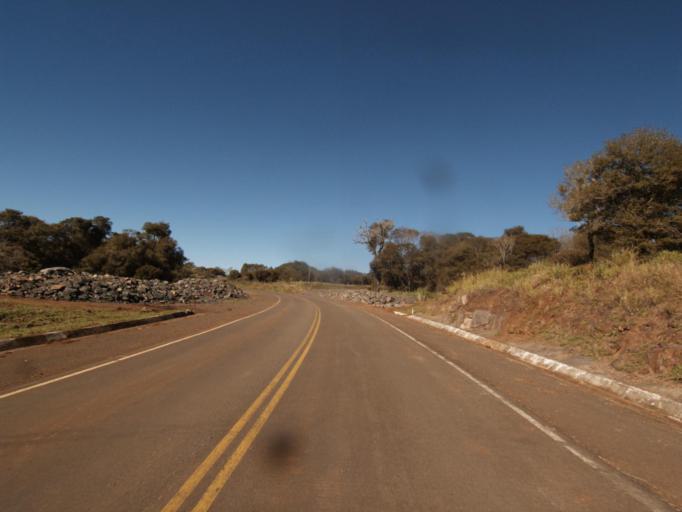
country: AR
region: Misiones
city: Bernardo de Irigoyen
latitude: -26.6137
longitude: -53.7162
